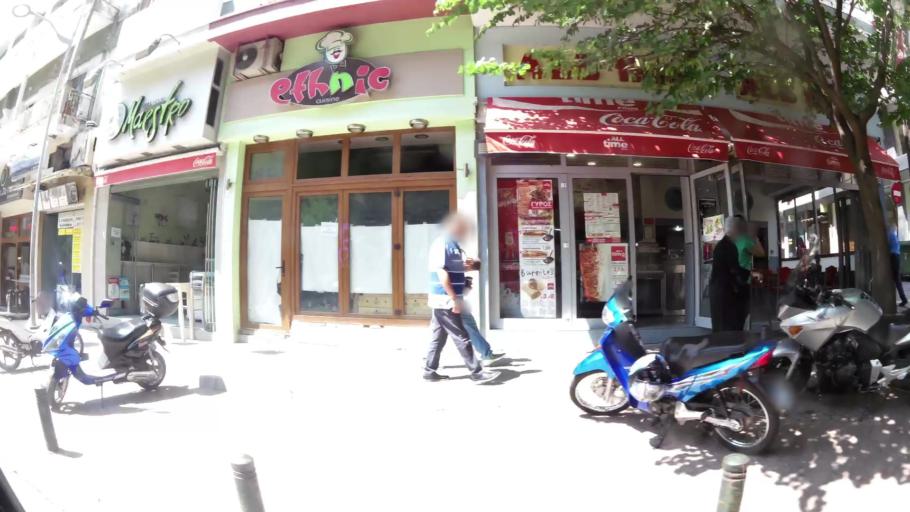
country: GR
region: West Macedonia
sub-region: Nomos Kozanis
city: Kozani
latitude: 40.3018
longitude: 21.7858
